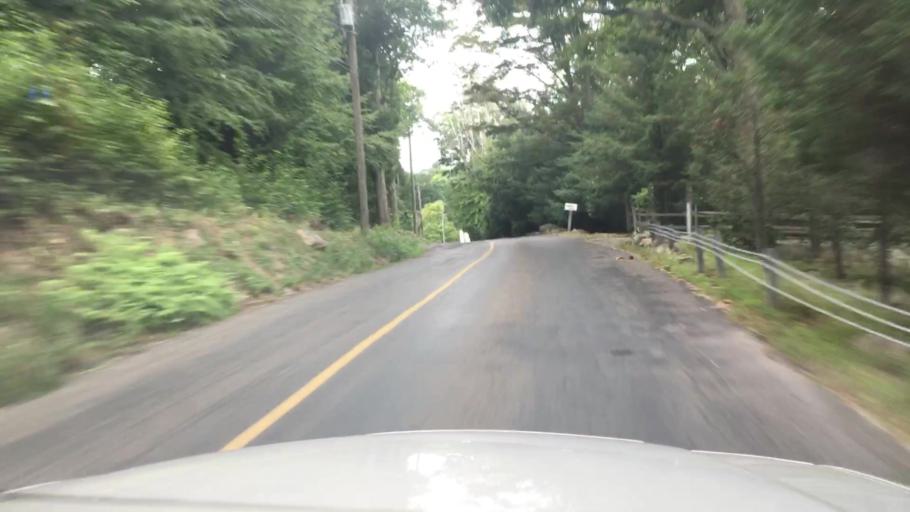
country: US
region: Connecticut
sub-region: Middlesex County
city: Deep River Center
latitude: 41.3873
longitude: -72.4124
